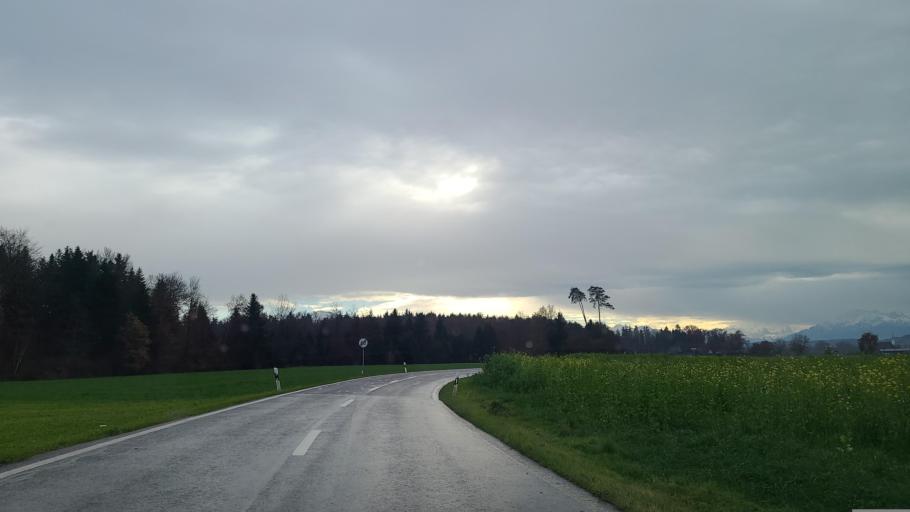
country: CH
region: Aargau
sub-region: Bezirk Muri
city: Sins
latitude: 47.2199
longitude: 8.4139
